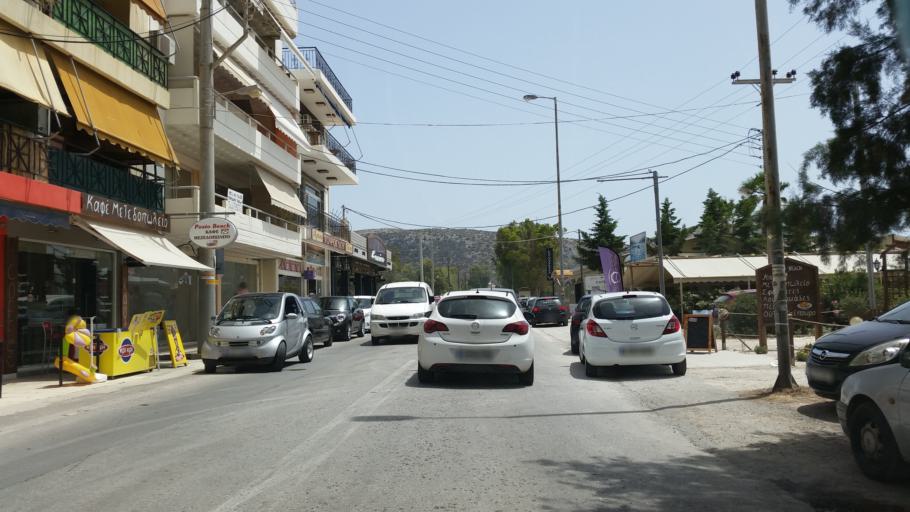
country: GR
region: Attica
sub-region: Nomarchia Anatolikis Attikis
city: Palaia Fokaia
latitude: 37.7233
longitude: 23.9456
